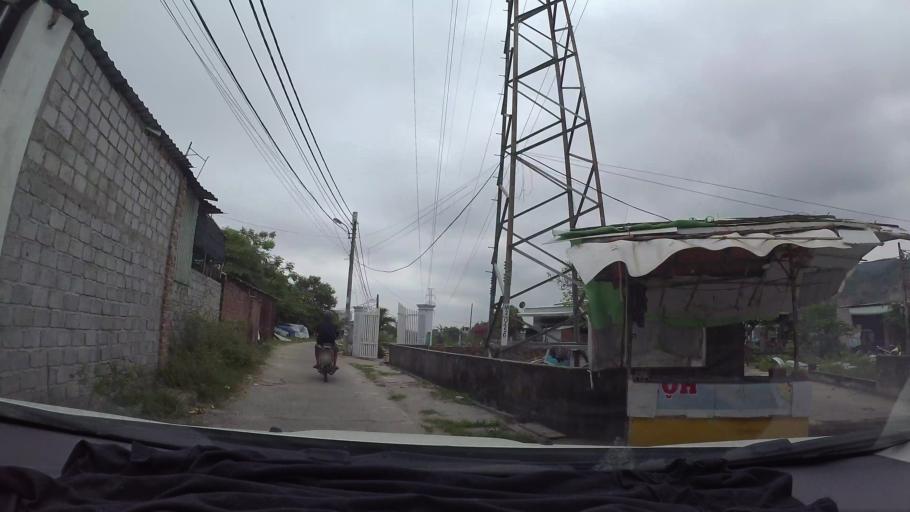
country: VN
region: Da Nang
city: Lien Chieu
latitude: 16.0476
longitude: 108.1697
